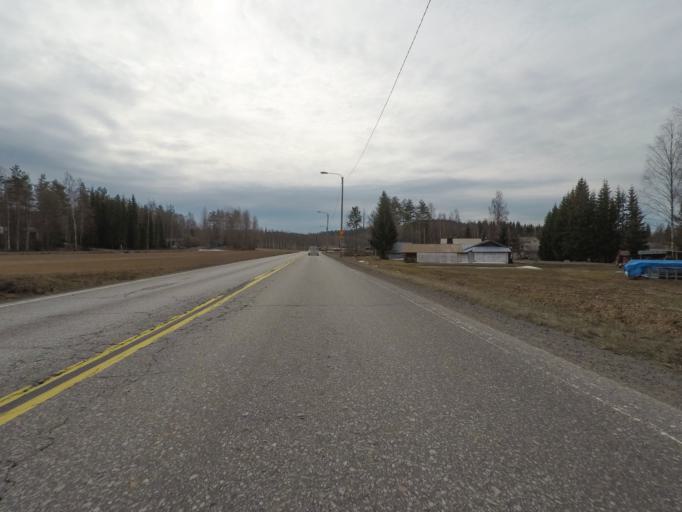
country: FI
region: Central Finland
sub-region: Jyvaeskylae
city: Toivakka
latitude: 62.0730
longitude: 26.0421
